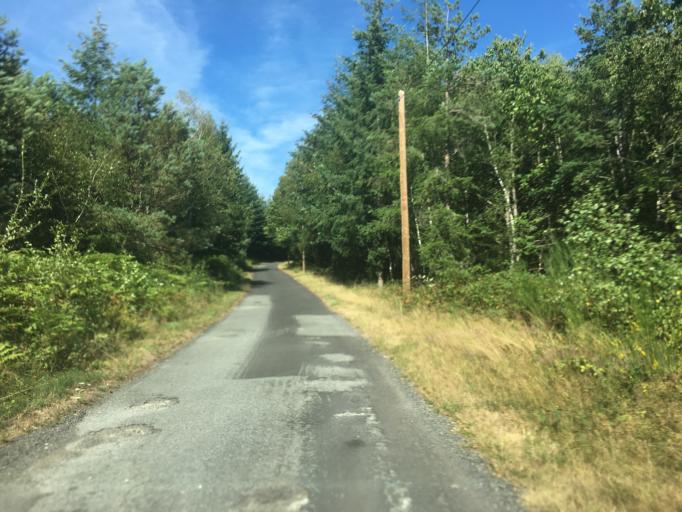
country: FR
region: Limousin
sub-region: Departement de la Correze
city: Egletons
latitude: 45.4228
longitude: 2.1474
